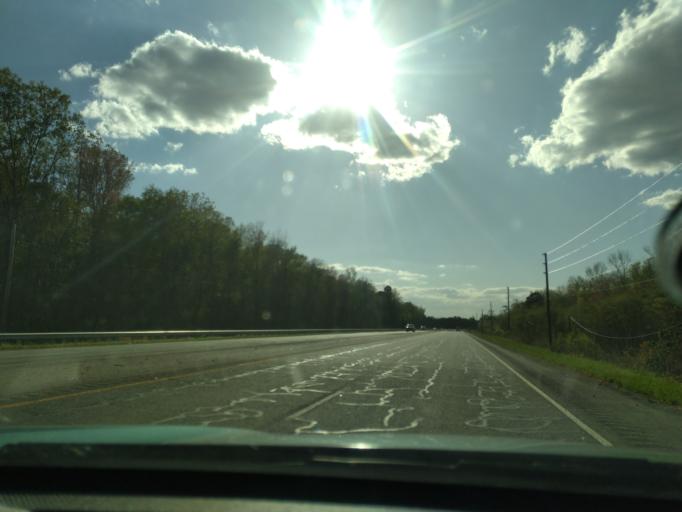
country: US
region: South Carolina
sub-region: Williamsburg County
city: Kingstree
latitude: 33.6578
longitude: -79.8650
